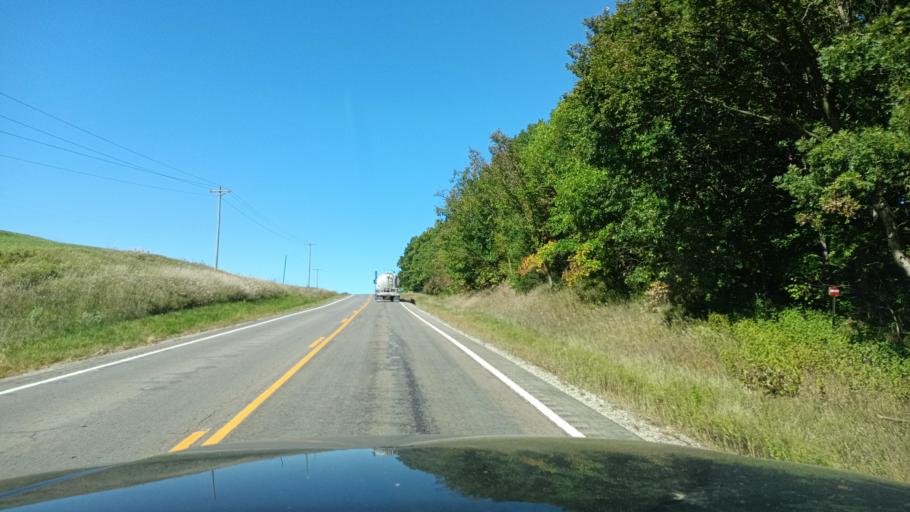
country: US
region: Missouri
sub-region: Scotland County
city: Memphis
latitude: 40.4541
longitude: -92.0027
